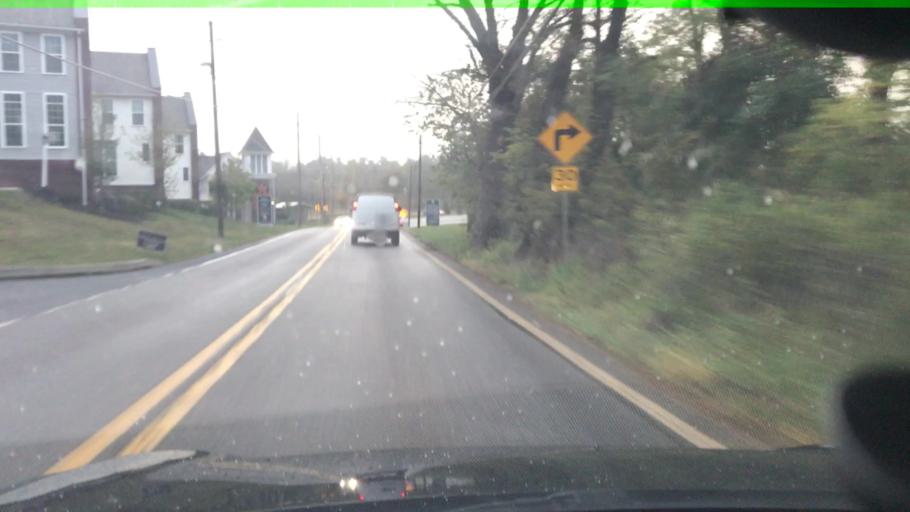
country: US
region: Pennsylvania
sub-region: Cumberland County
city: Shiremanstown
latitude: 40.1926
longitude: -76.9396
